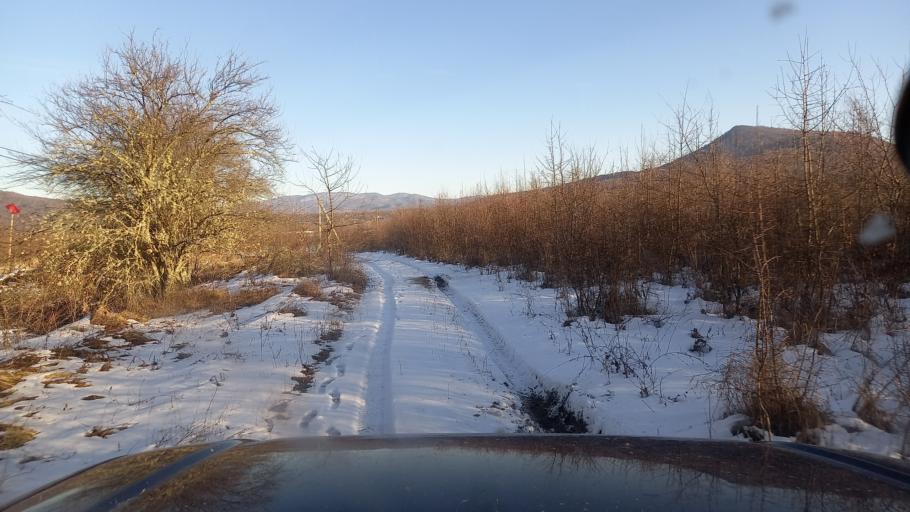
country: RU
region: Adygeya
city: Kamennomostskiy
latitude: 44.2264
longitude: 40.1668
